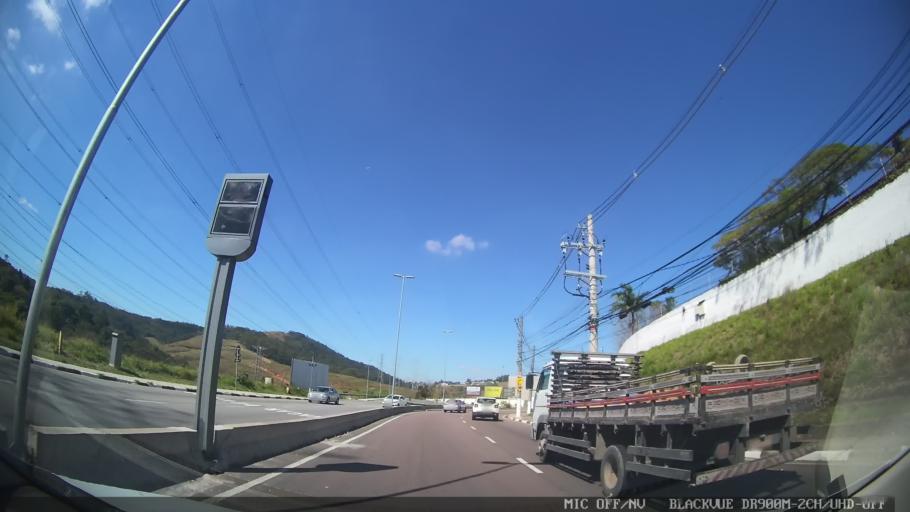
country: BR
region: Sao Paulo
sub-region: Carapicuiba
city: Carapicuiba
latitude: -23.4800
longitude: -46.8322
